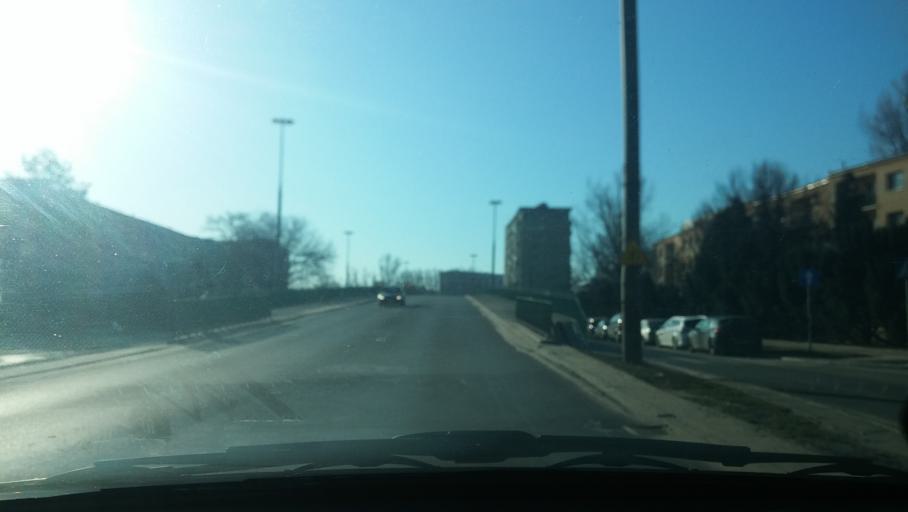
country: PL
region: Masovian Voivodeship
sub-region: Warszawa
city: Praga Poludnie
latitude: 52.2301
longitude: 21.0622
